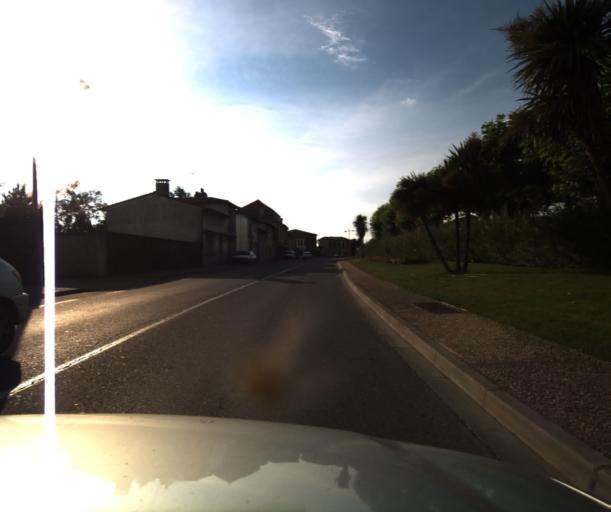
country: FR
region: Midi-Pyrenees
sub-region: Departement du Tarn-et-Garonne
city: Castelsarrasin
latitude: 44.0392
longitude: 1.1034
